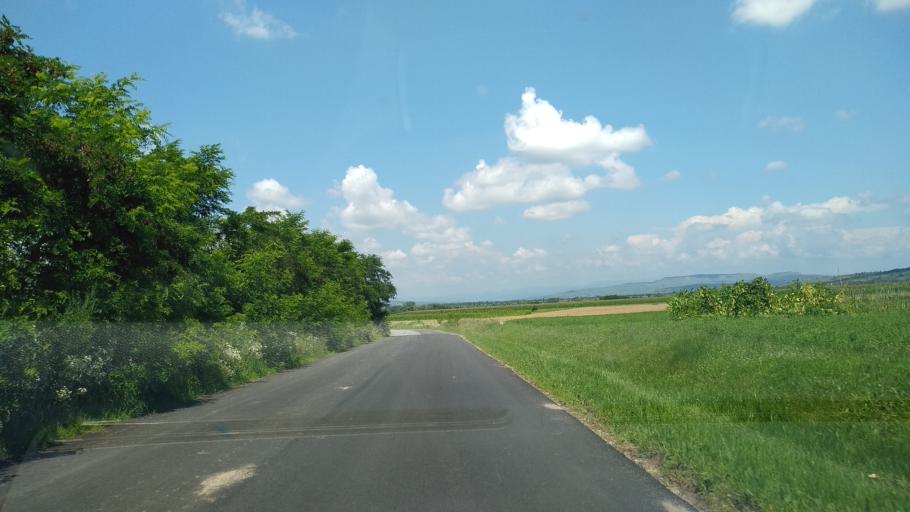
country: RO
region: Hunedoara
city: Berca
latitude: 45.6369
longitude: 23.0319
